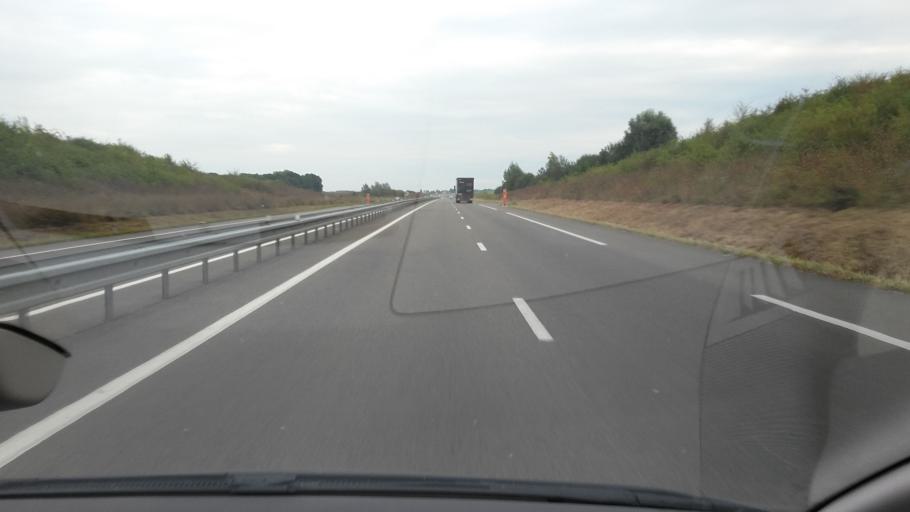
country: FR
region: Champagne-Ardenne
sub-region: Departement des Ardennes
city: Rethel
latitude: 49.5740
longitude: 4.4779
